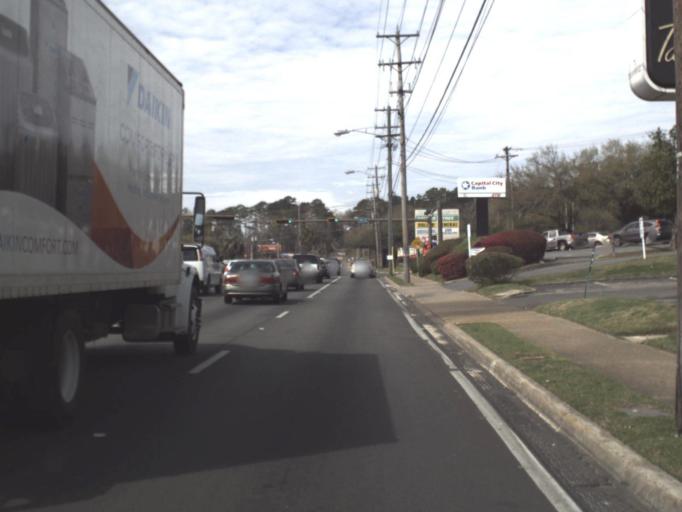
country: US
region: Florida
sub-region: Leon County
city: Tallahassee
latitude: 30.4492
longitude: -84.3124
